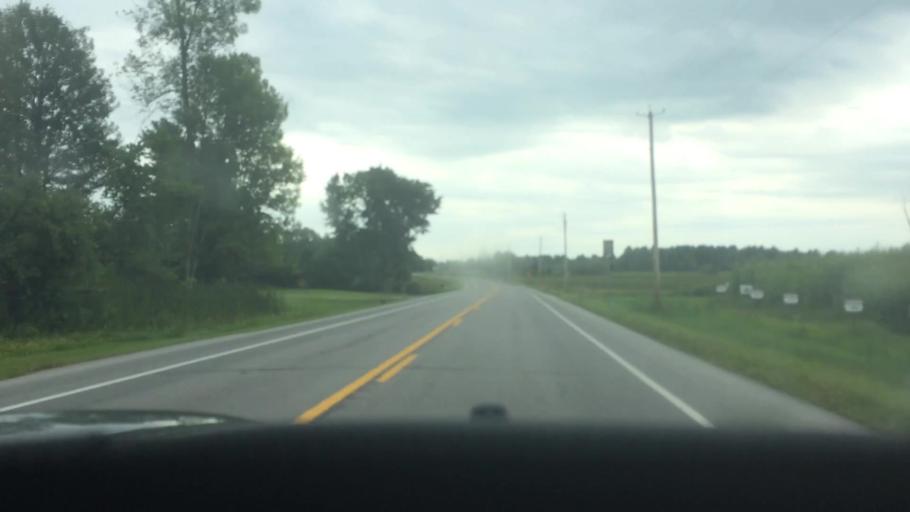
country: US
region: New York
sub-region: St. Lawrence County
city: Ogdensburg
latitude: 44.5815
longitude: -75.3698
